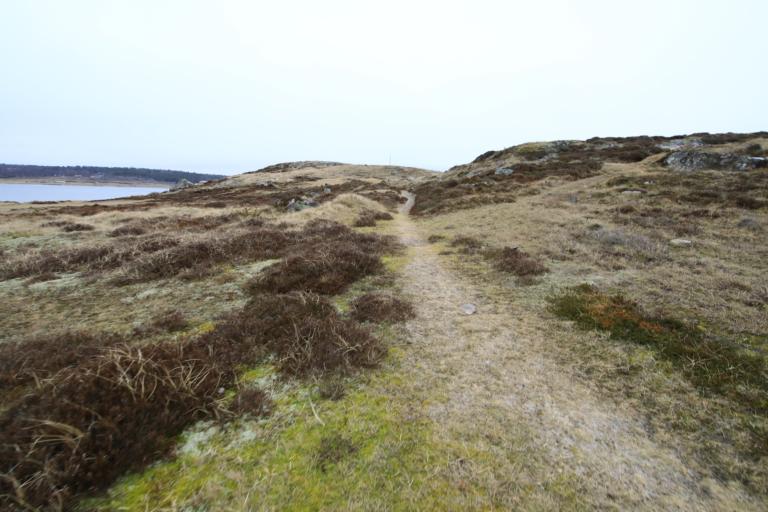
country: SE
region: Halland
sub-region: Kungsbacka Kommun
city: Frillesas
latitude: 57.2463
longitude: 12.1206
